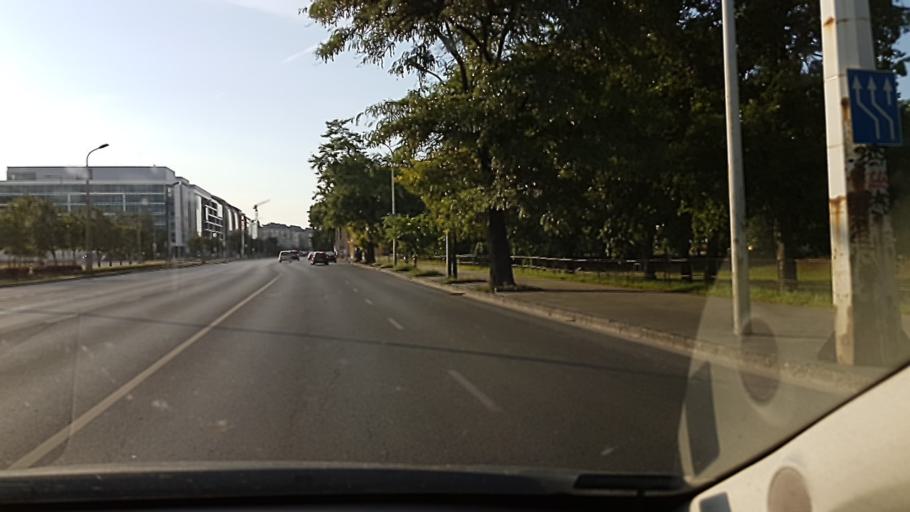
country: HU
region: Budapest
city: Budapest IX. keruelet
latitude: 47.4696
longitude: 19.0747
